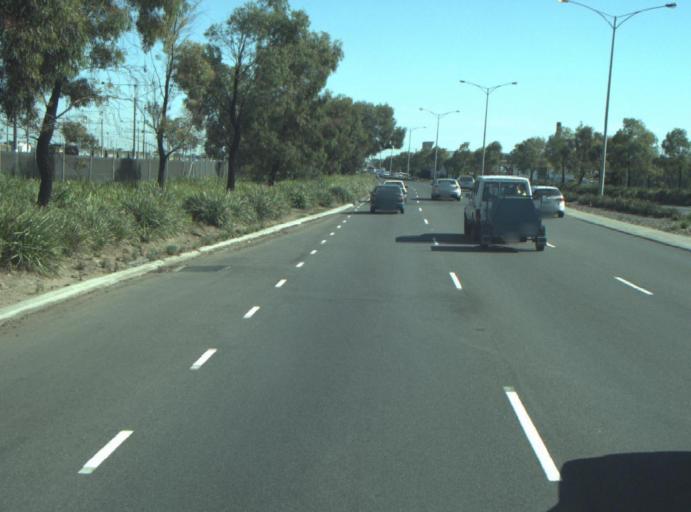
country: AU
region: Victoria
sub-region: Greater Geelong
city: Bell Park
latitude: -38.1195
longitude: 144.3534
